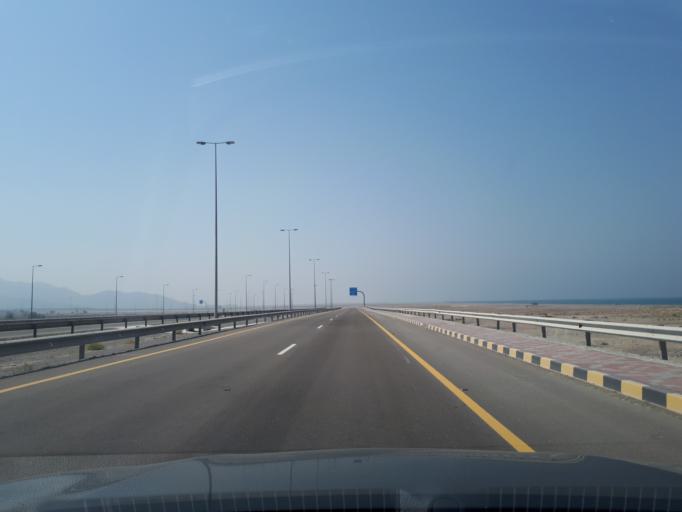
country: AE
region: Al Fujayrah
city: Al Fujayrah
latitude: 24.9460
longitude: 56.3810
